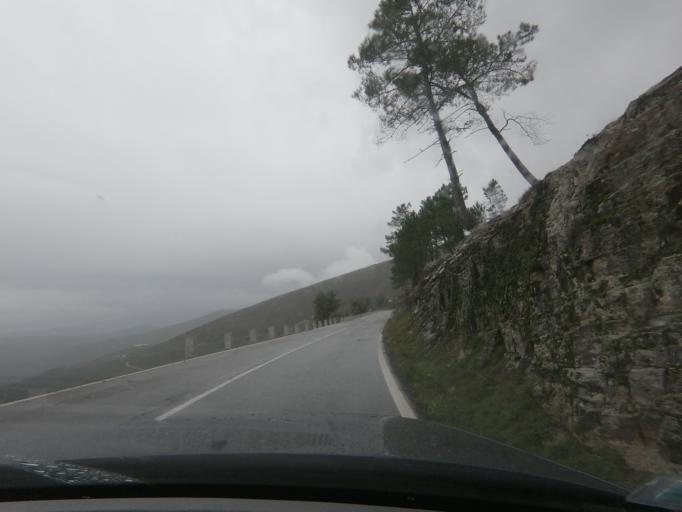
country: PT
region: Vila Real
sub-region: Mondim de Basto
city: Mondim de Basto
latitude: 41.3448
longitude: -7.8733
